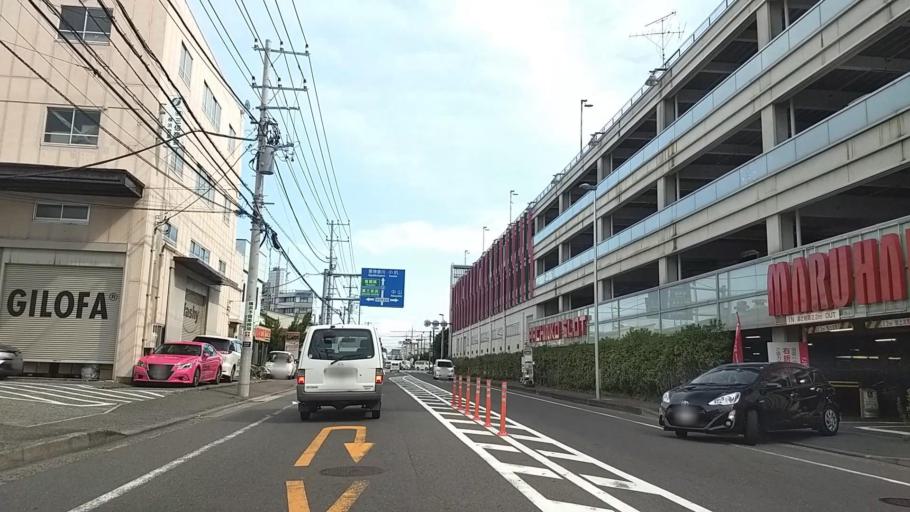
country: JP
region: Kanagawa
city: Yokohama
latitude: 35.5185
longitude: 139.5740
